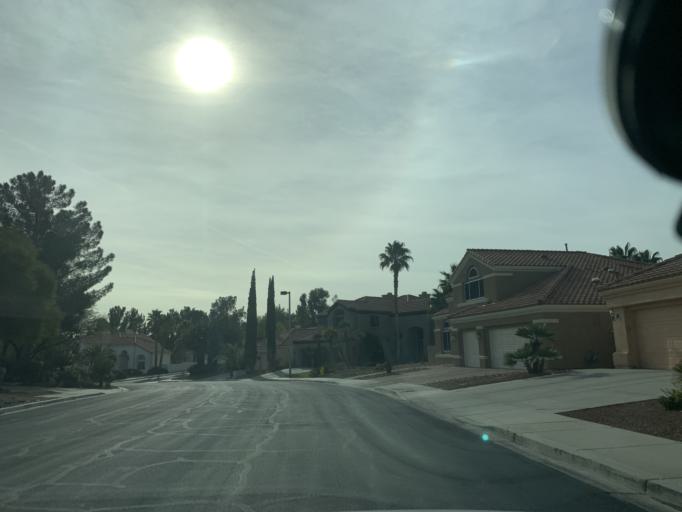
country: US
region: Nevada
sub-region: Clark County
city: Summerlin South
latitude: 36.1523
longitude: -115.3028
